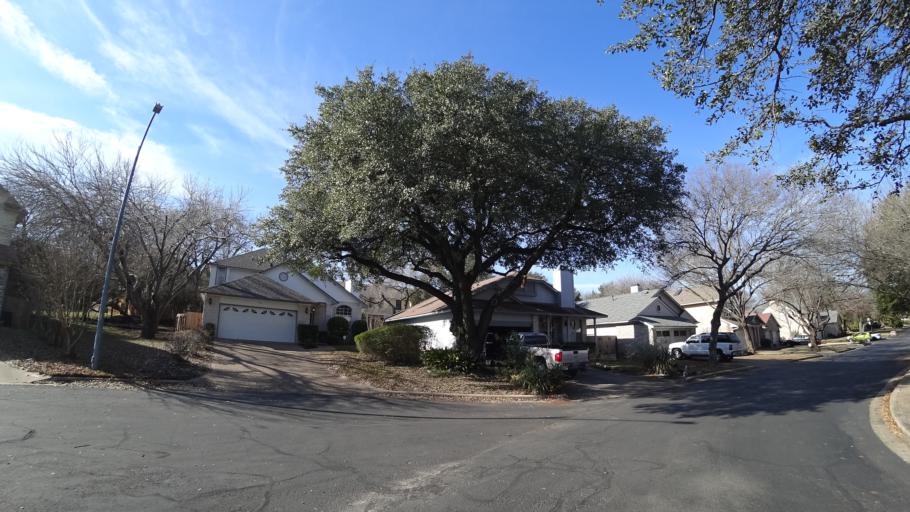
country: US
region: Texas
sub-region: Travis County
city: Wells Branch
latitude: 30.3952
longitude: -97.6909
